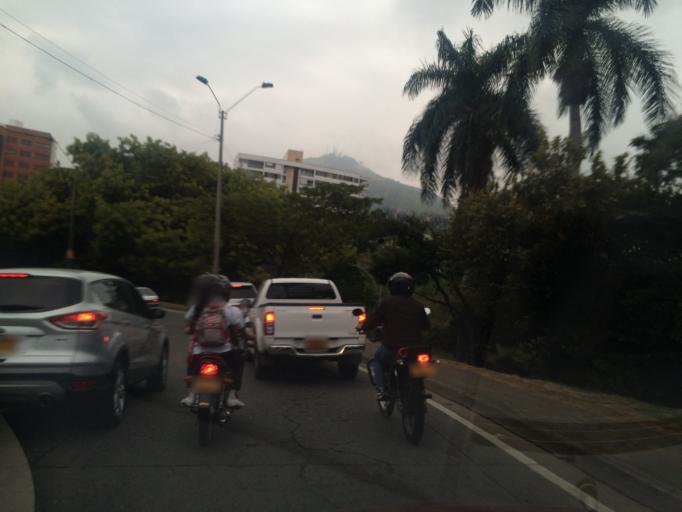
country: CO
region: Valle del Cauca
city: Cali
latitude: 3.4470
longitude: -76.5459
